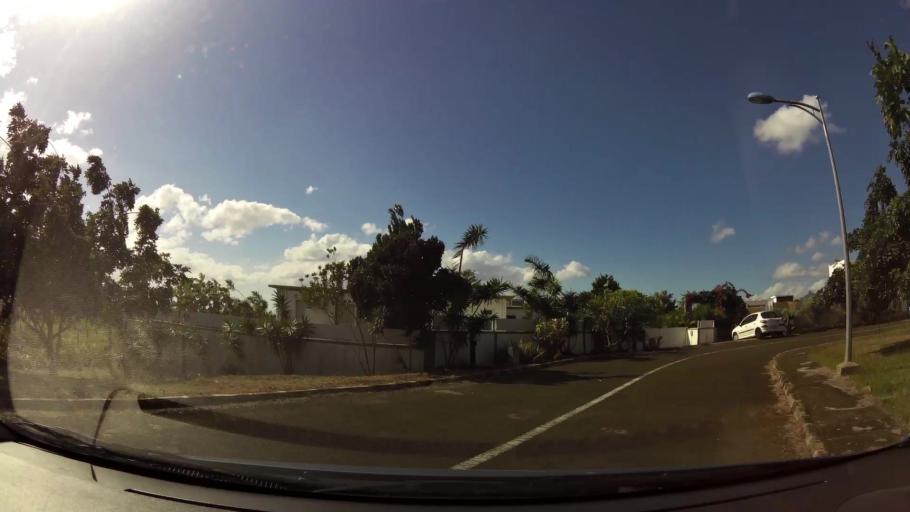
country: MU
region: Black River
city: Albion
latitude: -20.2170
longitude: 57.4127
